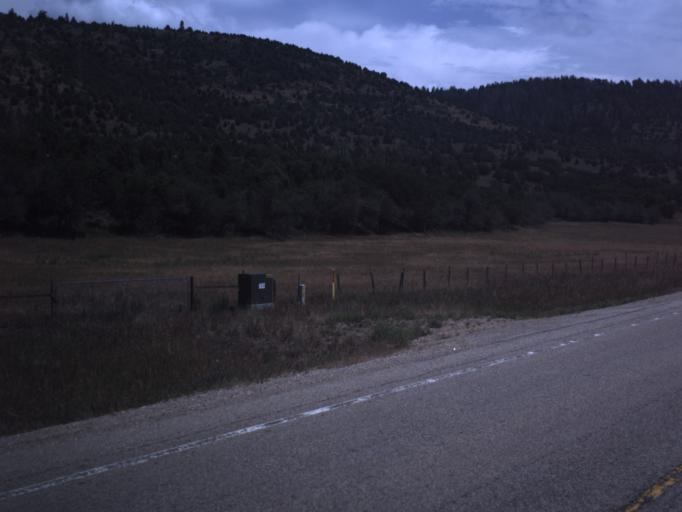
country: US
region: Utah
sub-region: Summit County
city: Francis
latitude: 40.5591
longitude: -111.1230
